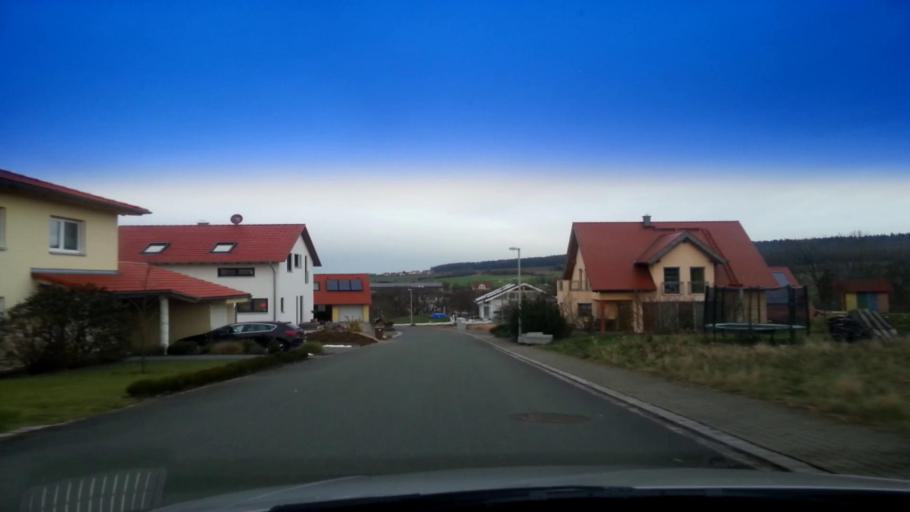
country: DE
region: Bavaria
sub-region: Upper Franconia
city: Litzendorf
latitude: 49.9095
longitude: 11.0176
